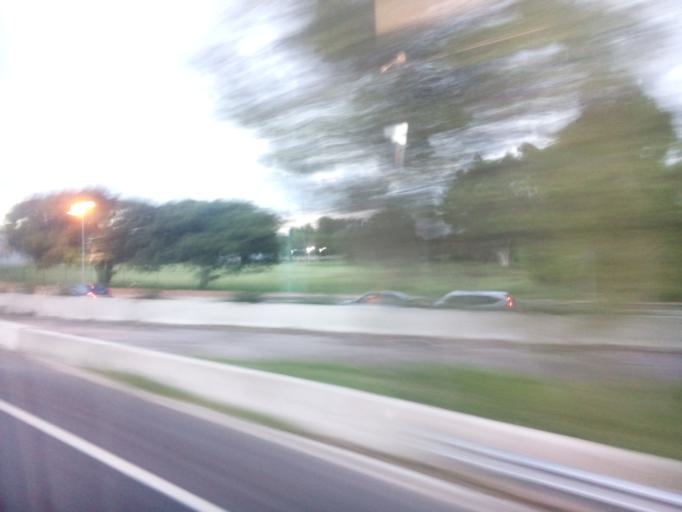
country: AR
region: Buenos Aires F.D.
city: Colegiales
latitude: -34.5508
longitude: -58.4333
